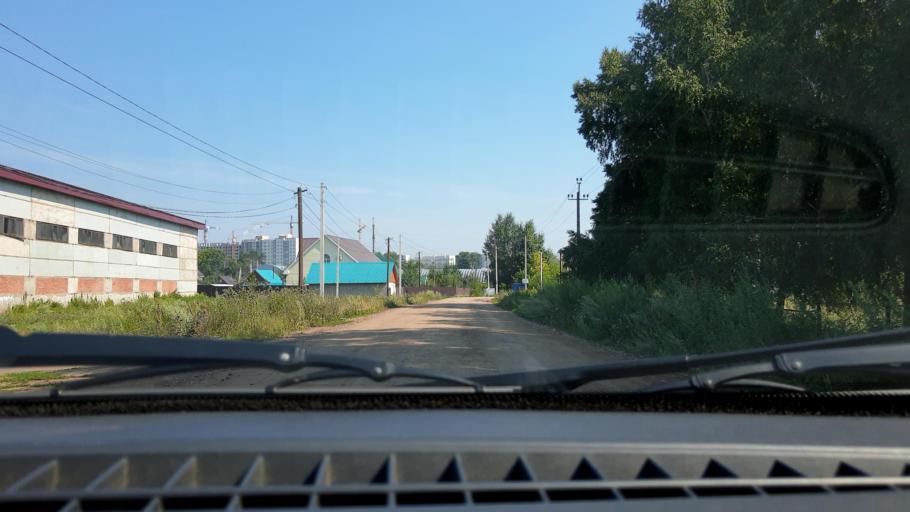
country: RU
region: Bashkortostan
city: Mikhaylovka
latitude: 54.7843
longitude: 55.8423
